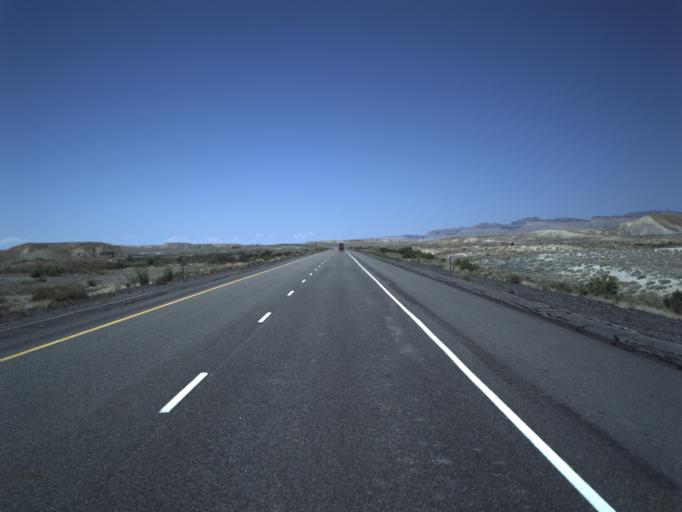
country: US
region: Utah
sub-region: Grand County
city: Moab
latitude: 38.9410
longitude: -109.5117
